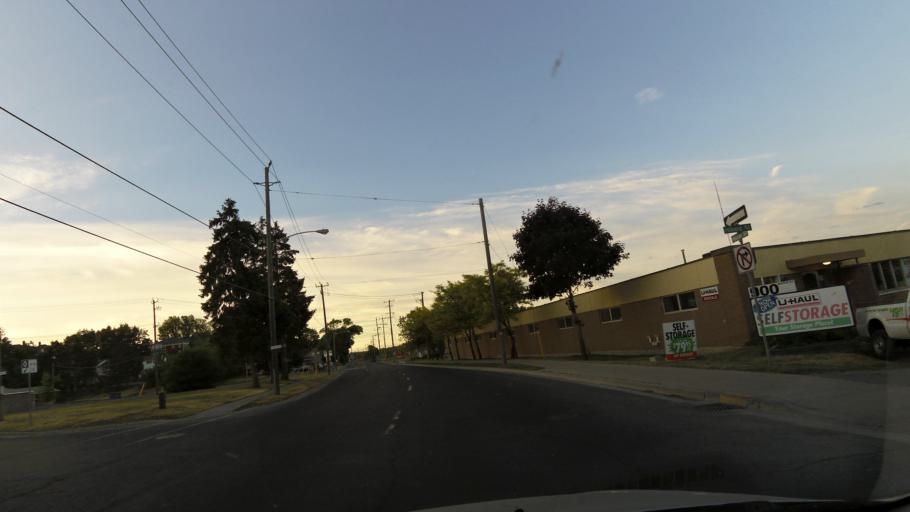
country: CA
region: Ontario
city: Peterborough
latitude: 44.3212
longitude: -78.3162
